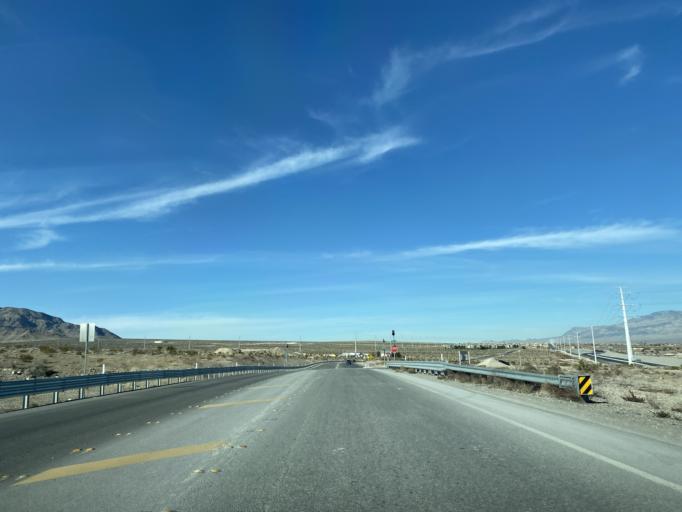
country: US
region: Nevada
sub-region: Clark County
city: Summerlin South
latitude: 36.2599
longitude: -115.3292
